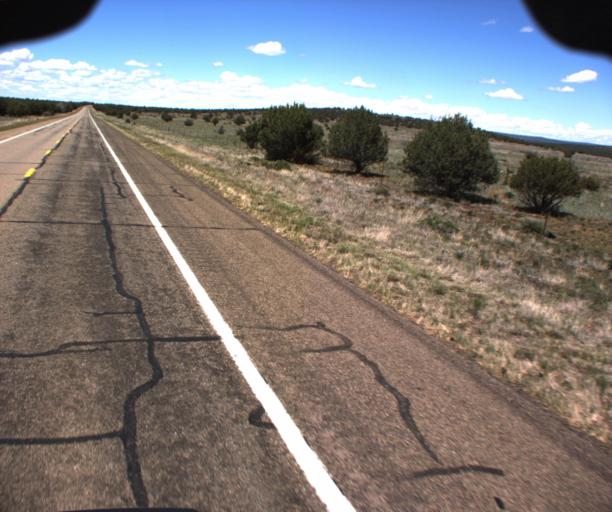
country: US
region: Arizona
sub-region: Yavapai County
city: Paulden
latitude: 35.1517
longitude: -112.4505
